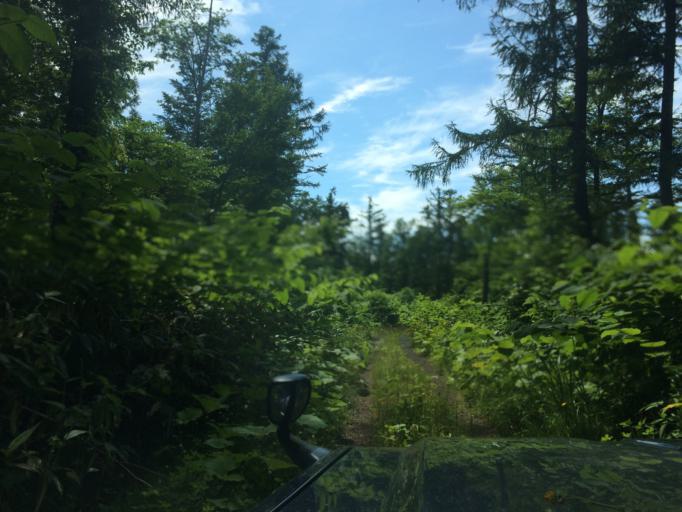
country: JP
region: Hokkaido
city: Niseko Town
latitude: 42.8652
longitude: 140.7986
